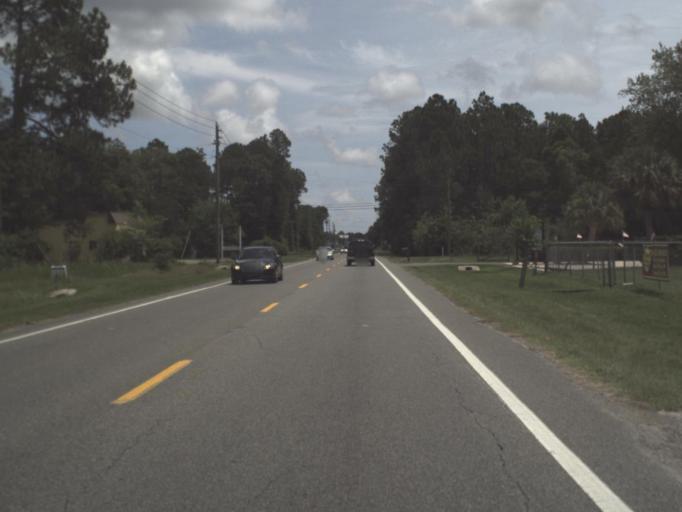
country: US
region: Florida
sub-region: Nassau County
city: Yulee
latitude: 30.6394
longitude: -81.6099
